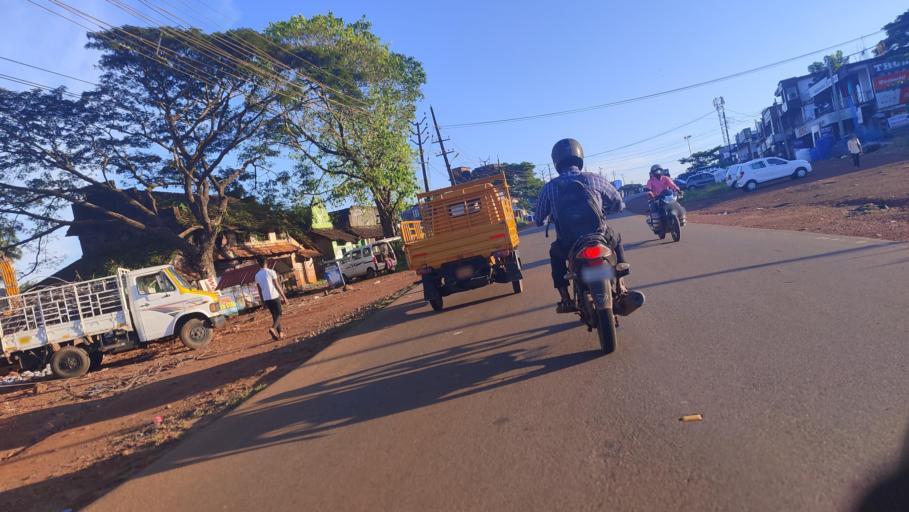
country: IN
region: Kerala
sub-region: Kasaragod District
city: Kasaragod
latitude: 12.4812
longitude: 75.0578
